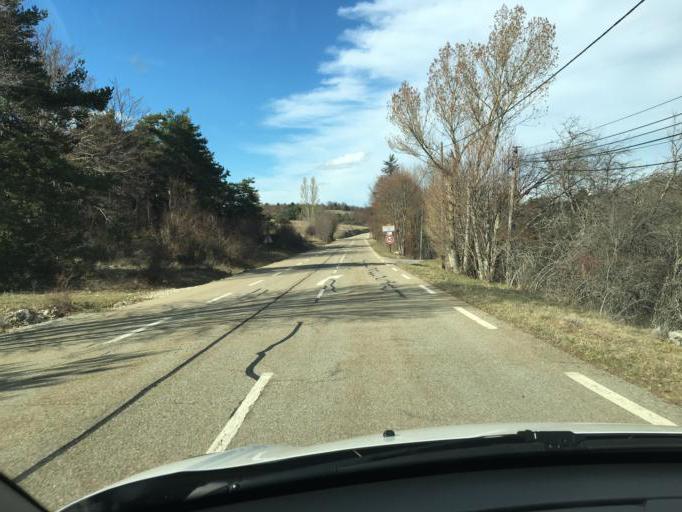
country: FR
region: Provence-Alpes-Cote d'Azur
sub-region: Departement du Vaucluse
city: Saint-Saturnin-les-Apt
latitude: 43.9818
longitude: 5.4724
